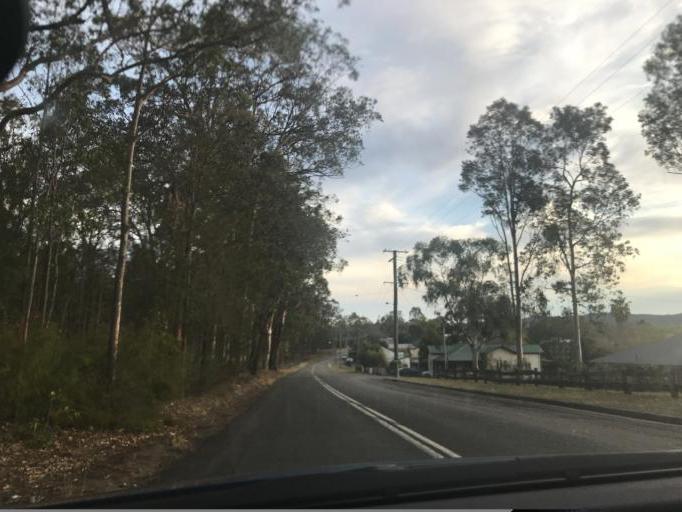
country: AU
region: New South Wales
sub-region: Cessnock
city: Cessnock
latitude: -32.9021
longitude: 151.2916
